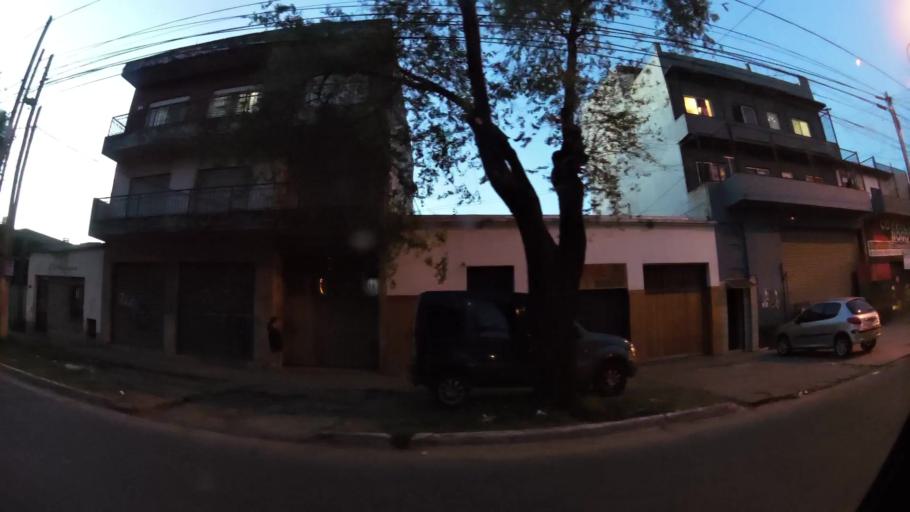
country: AR
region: Buenos Aires
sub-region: Partido de Quilmes
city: Quilmes
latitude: -34.7656
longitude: -58.1987
